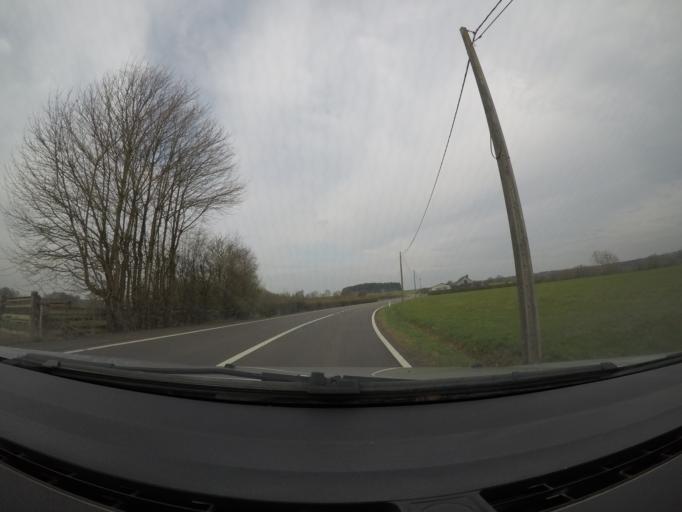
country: BE
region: Wallonia
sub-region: Province du Luxembourg
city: Tintigny
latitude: 49.7177
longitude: 5.4770
